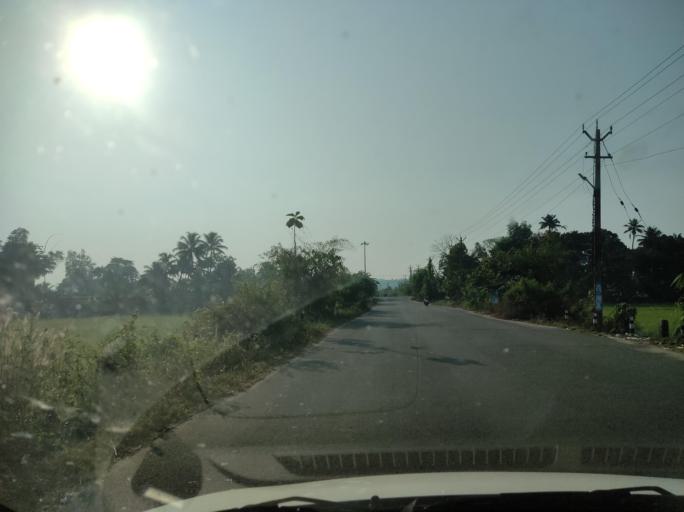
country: IN
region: Kerala
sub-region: Kottayam
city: Kottayam
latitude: 9.5673
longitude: 76.5049
